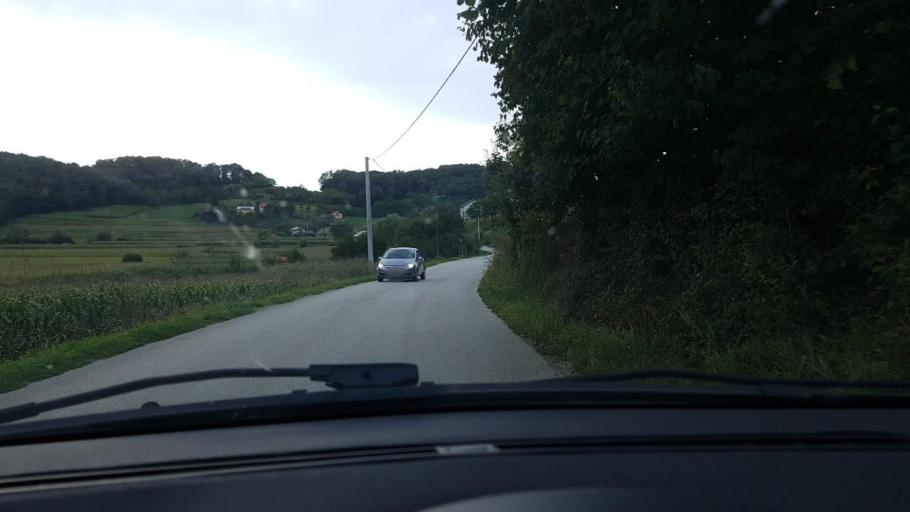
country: HR
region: Krapinsko-Zagorska
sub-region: Grad Krapina
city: Krapina
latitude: 46.1539
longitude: 15.8428
